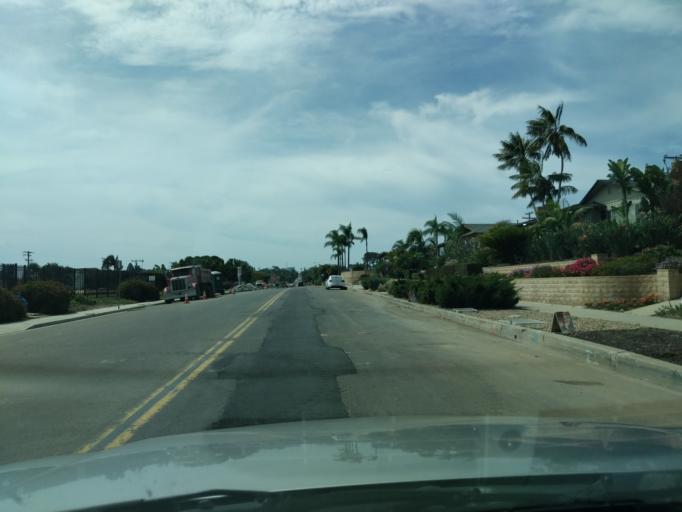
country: US
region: California
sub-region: San Diego County
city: Coronado
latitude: 32.7253
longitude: -117.2449
